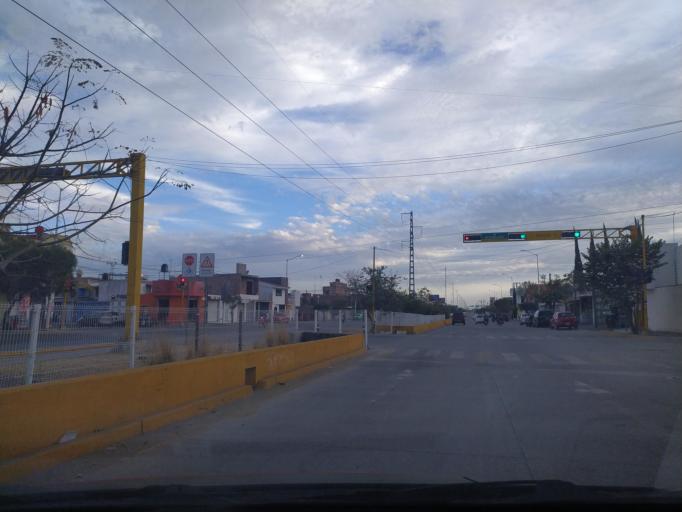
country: LA
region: Oudomxai
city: Muang La
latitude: 21.0277
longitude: 101.8695
